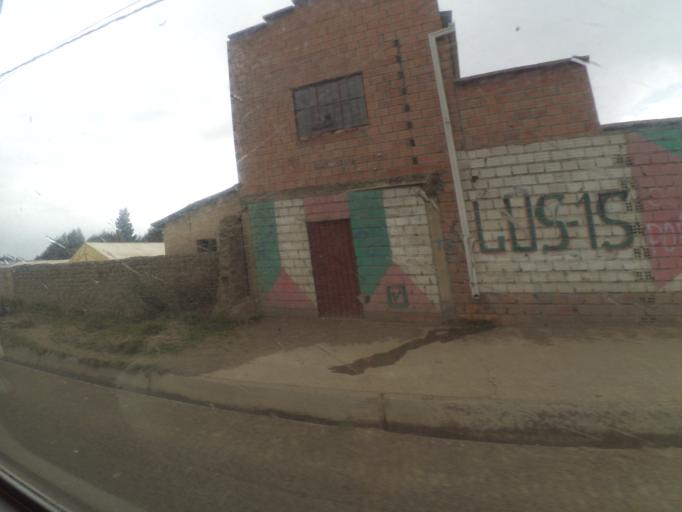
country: BO
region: La Paz
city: La Paz
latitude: -16.5714
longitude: -68.1749
